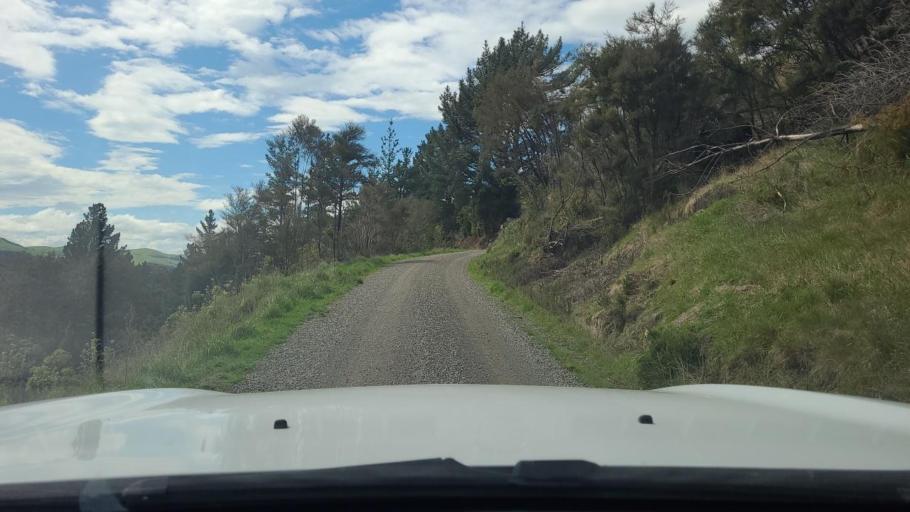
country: NZ
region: Wellington
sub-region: South Wairarapa District
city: Waipawa
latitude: -41.3440
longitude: 175.4087
